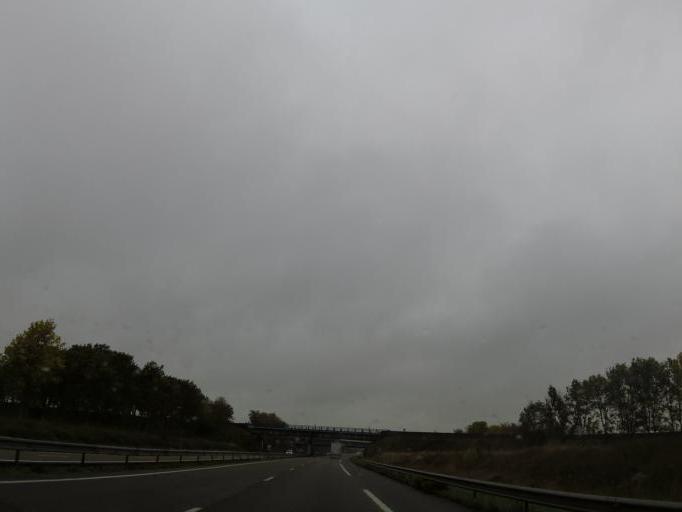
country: FR
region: Champagne-Ardenne
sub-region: Departement de la Marne
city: Fagnieres
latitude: 49.0532
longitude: 4.2895
